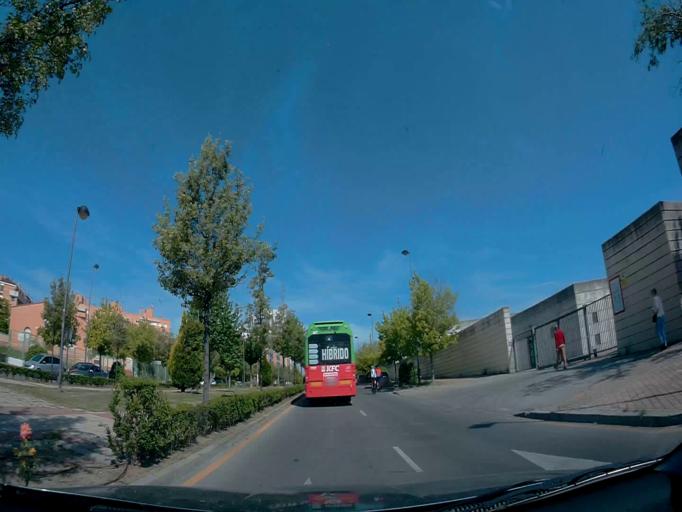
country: ES
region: Madrid
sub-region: Provincia de Madrid
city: Alcorcon
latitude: 40.3464
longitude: -3.8380
